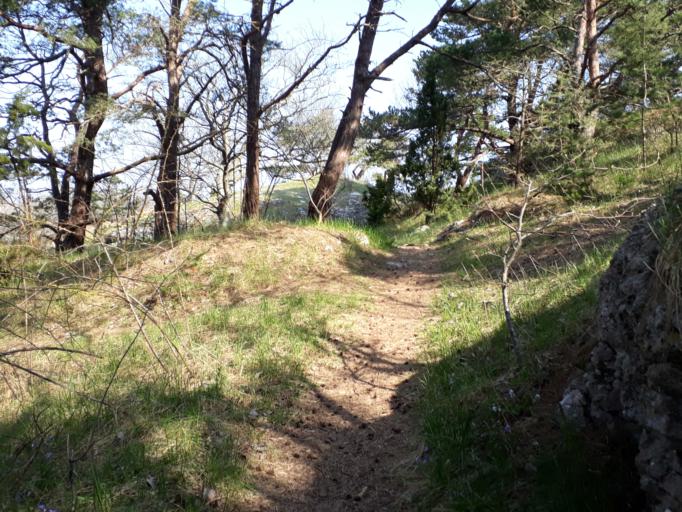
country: SE
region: Gotland
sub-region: Gotland
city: Visby
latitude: 57.6711
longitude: 18.3334
